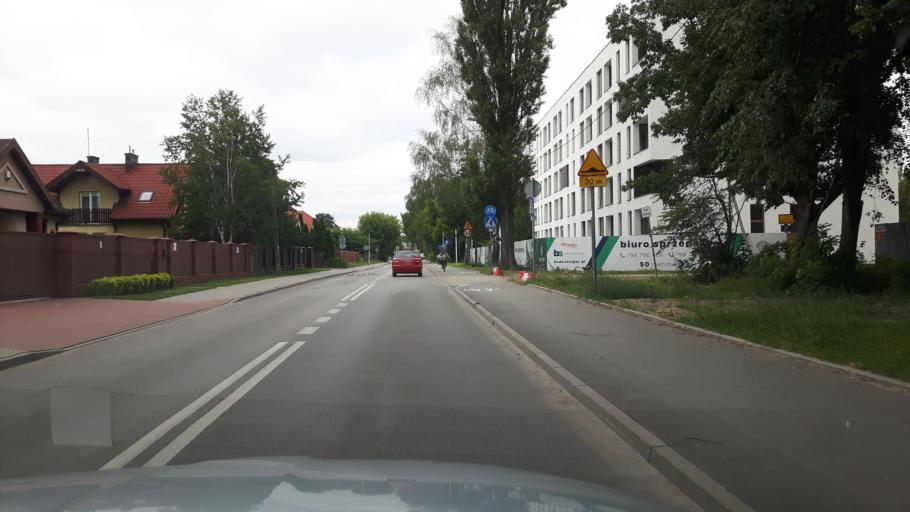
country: PL
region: Masovian Voivodeship
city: Zielonka
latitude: 52.3001
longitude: 21.1612
